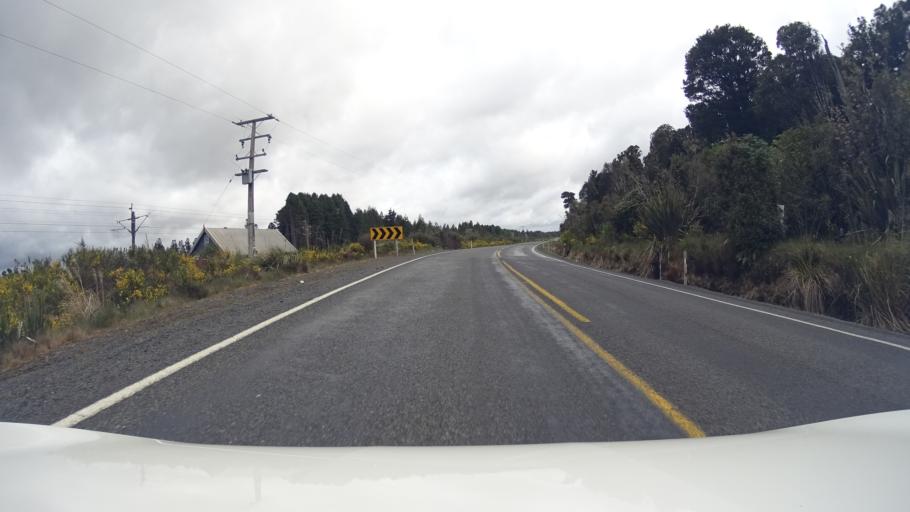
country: NZ
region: Manawatu-Wanganui
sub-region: Ruapehu District
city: Waiouru
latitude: -39.2556
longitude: 175.3879
